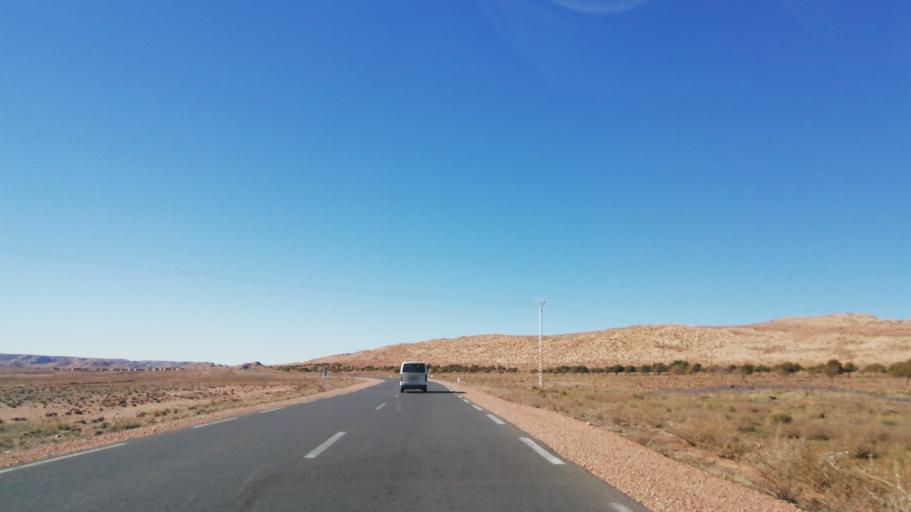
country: DZ
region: El Bayadh
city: El Bayadh
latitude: 33.6174
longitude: 1.1889
